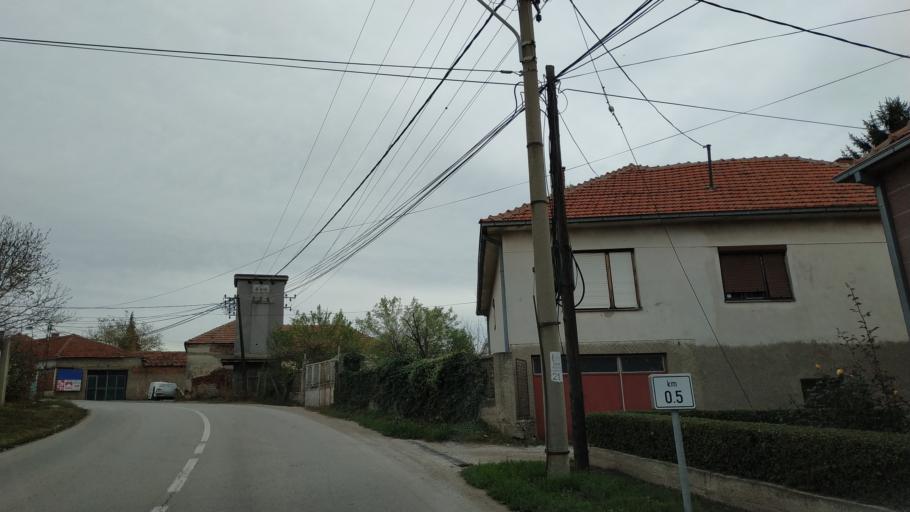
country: RS
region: Central Serbia
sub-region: Nisavski Okrug
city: Nis
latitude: 43.3617
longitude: 21.9596
